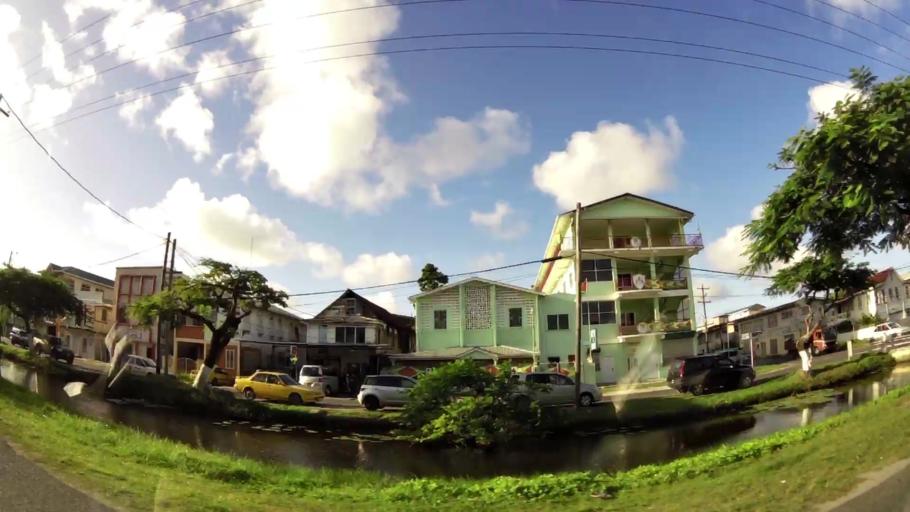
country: GY
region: Demerara-Mahaica
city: Georgetown
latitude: 6.8067
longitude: -58.1545
